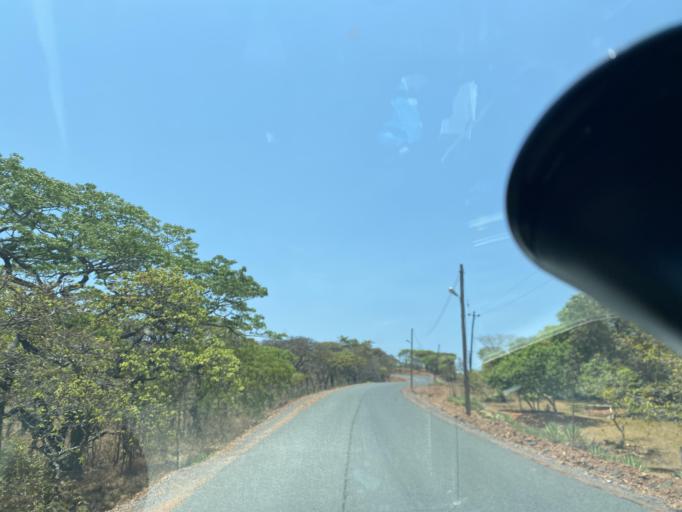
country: ZM
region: Lusaka
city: Kafue
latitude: -15.8660
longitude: 28.4492
